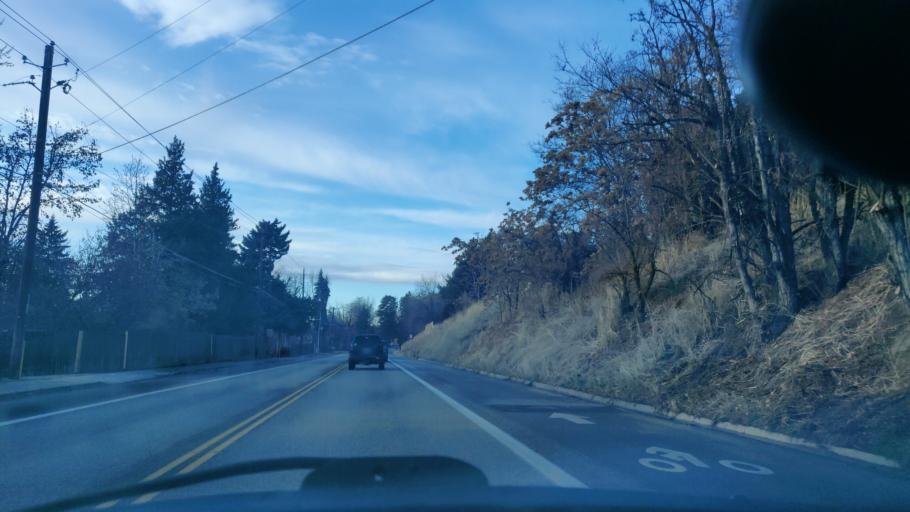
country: US
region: Idaho
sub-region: Ada County
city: Boise
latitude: 43.6417
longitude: -116.2112
